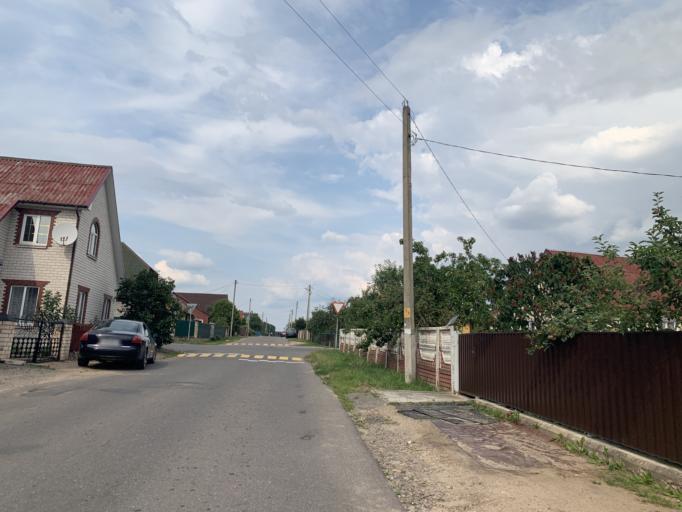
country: BY
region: Minsk
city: Nyasvizh
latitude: 53.2071
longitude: 26.6848
